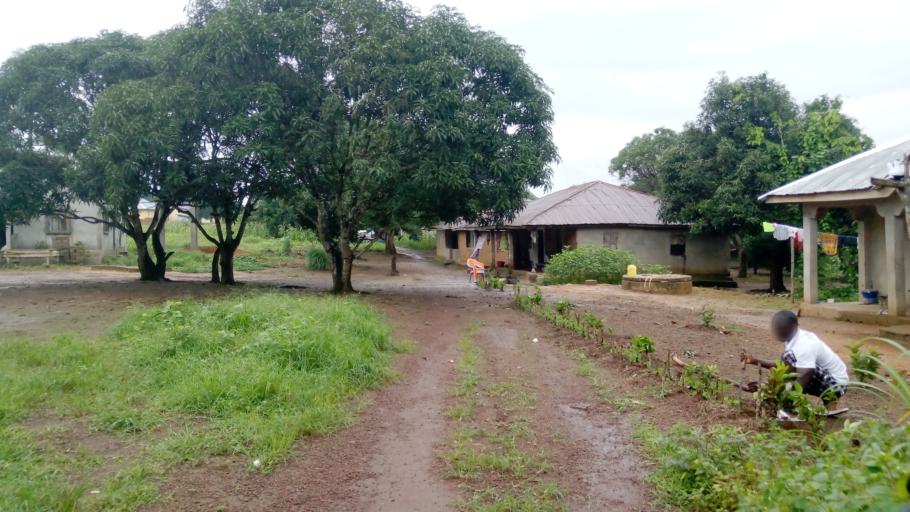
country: SL
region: Southern Province
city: Rotifunk
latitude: 8.4877
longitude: -12.7478
